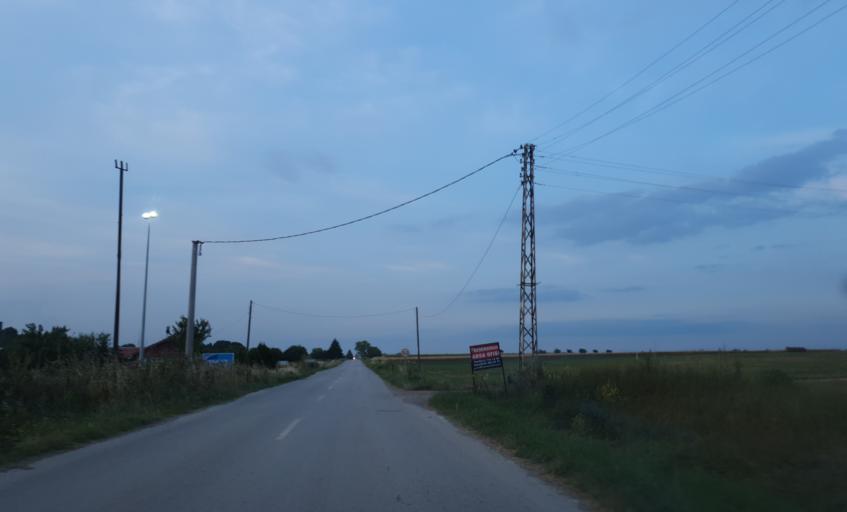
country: TR
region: Tekirdag
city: Beyazkoy
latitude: 41.3890
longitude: 27.6246
